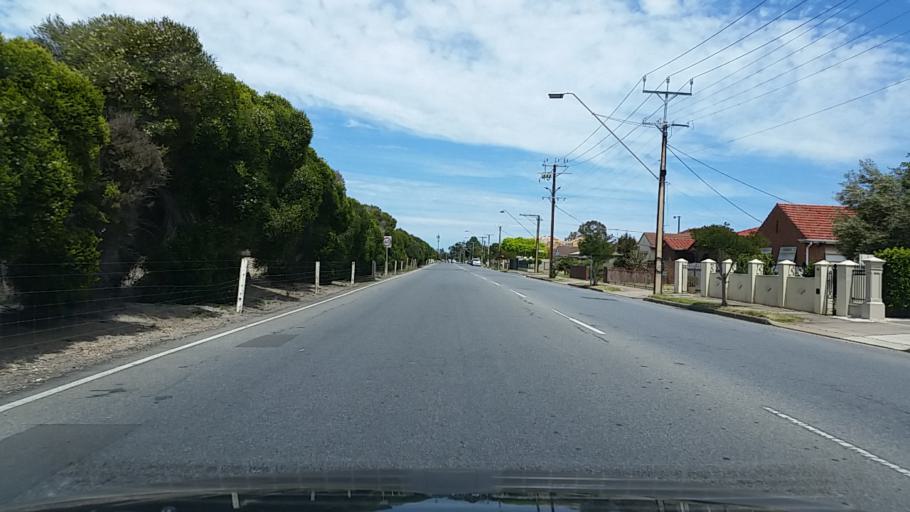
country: AU
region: South Australia
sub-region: Charles Sturt
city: Woodville West
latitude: -34.8858
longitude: 138.5191
